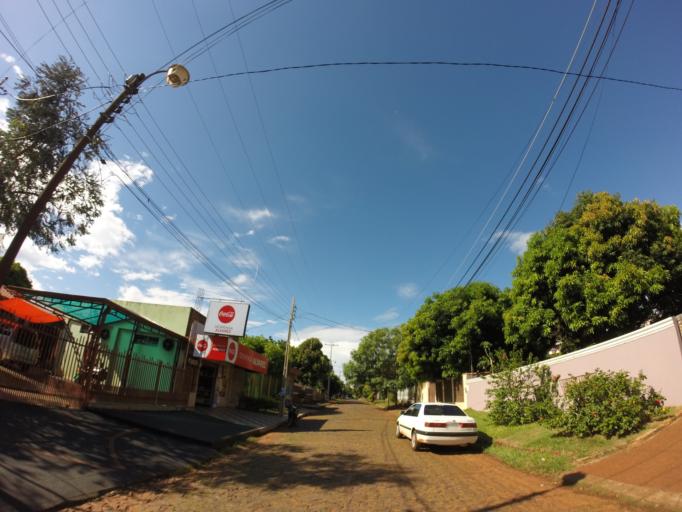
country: PY
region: Alto Parana
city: Ciudad del Este
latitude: -25.4073
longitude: -54.6260
